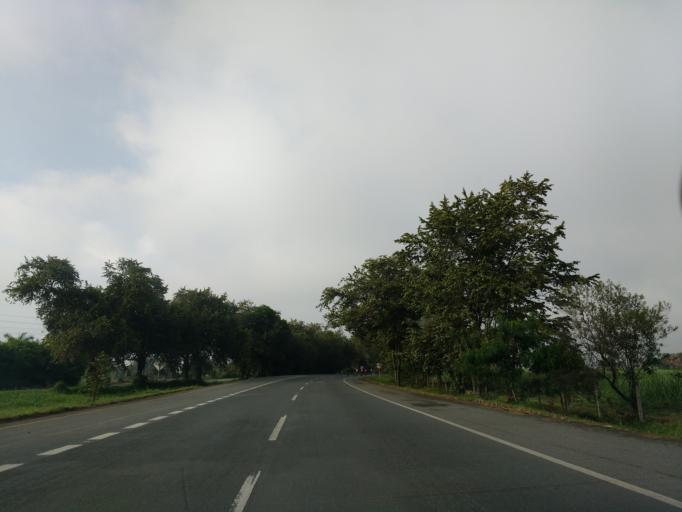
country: CO
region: Valle del Cauca
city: El Cerrito
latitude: 3.6631
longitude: -76.2928
